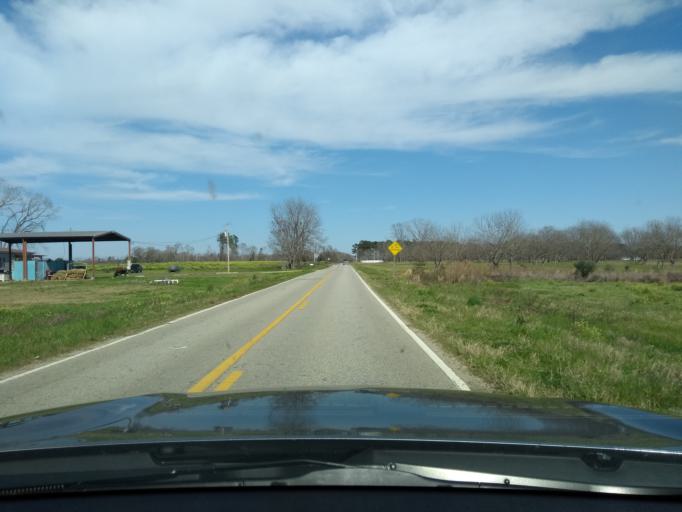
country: US
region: Georgia
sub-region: Bulloch County
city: Brooklet
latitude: 32.4589
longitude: -81.6580
